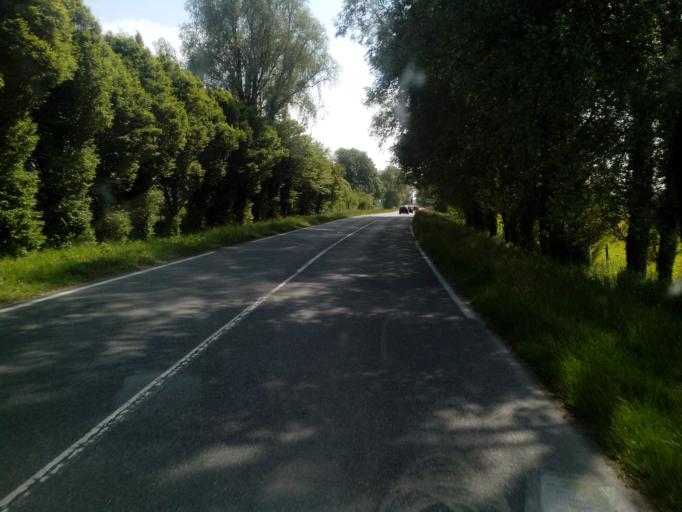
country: FR
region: Picardie
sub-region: Departement de la Somme
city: Rue
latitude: 50.2742
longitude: 1.6589
